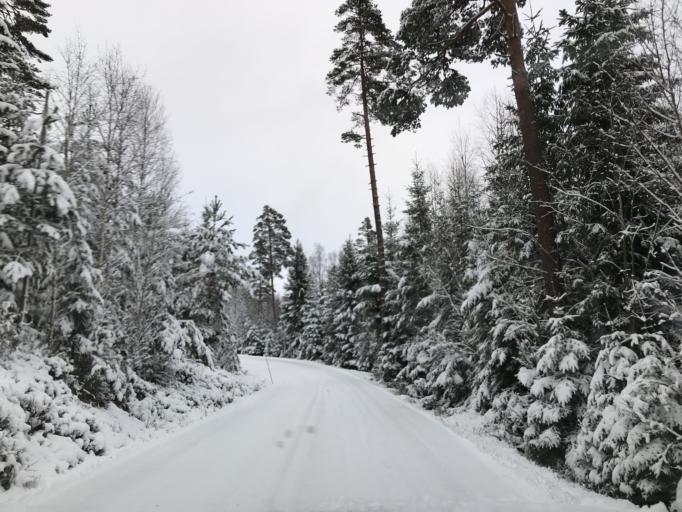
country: SE
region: Vaestra Goetaland
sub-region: Boras Kommun
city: Sandared
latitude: 57.8055
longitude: 12.7084
